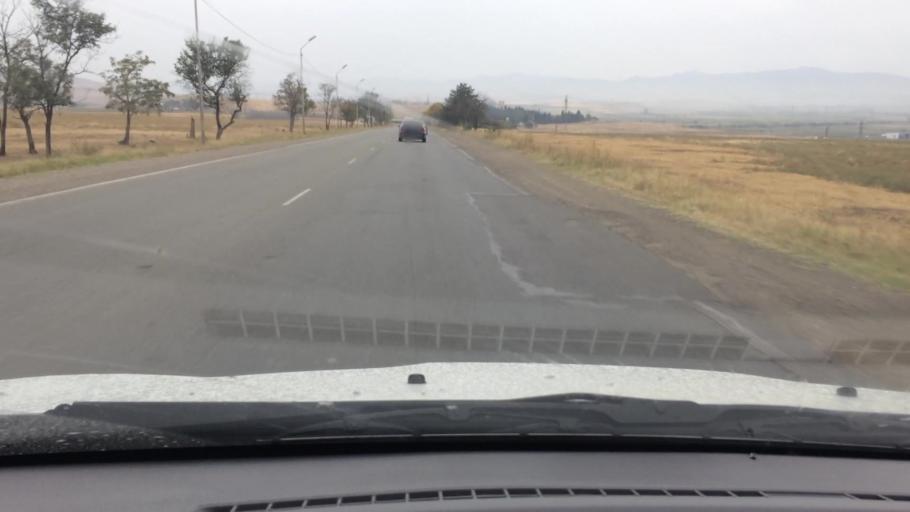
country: GE
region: Kvemo Kartli
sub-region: Marneuli
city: Marneuli
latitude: 41.5143
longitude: 44.7876
